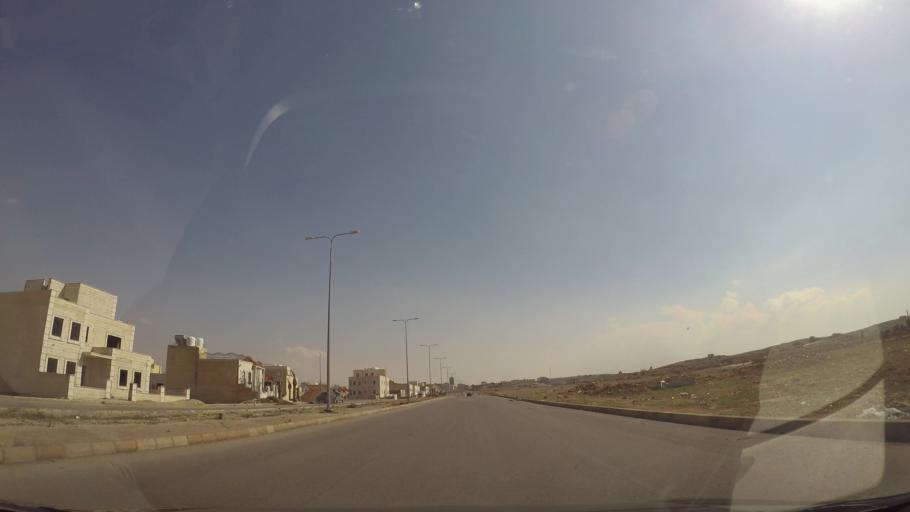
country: JO
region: Zarqa
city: Zarqa
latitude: 32.0589
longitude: 36.1134
